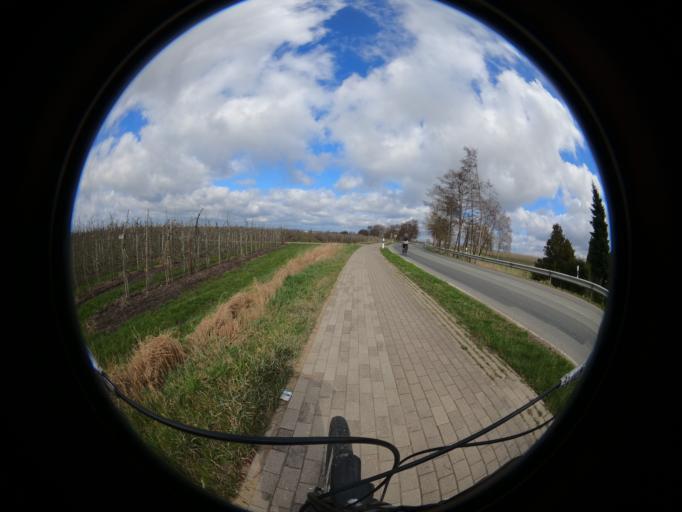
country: DE
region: Lower Saxony
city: Neu Wulmstorf
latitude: 53.4995
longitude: 9.7811
